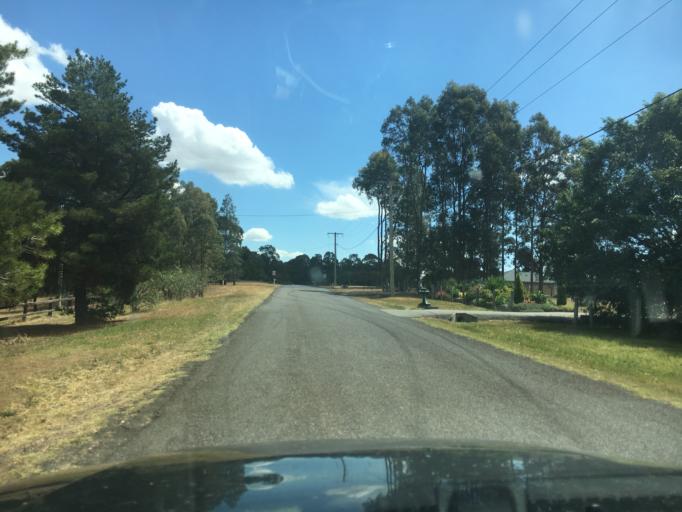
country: AU
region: New South Wales
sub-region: Singleton
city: Singleton
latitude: -32.5190
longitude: 151.1860
